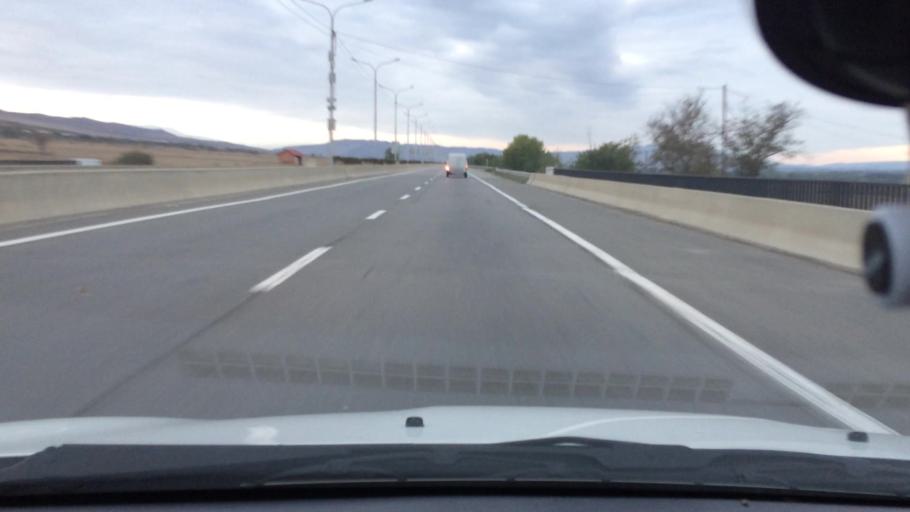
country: GE
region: Mtskheta-Mtianeti
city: Mtskheta
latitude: 41.8941
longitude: 44.6629
